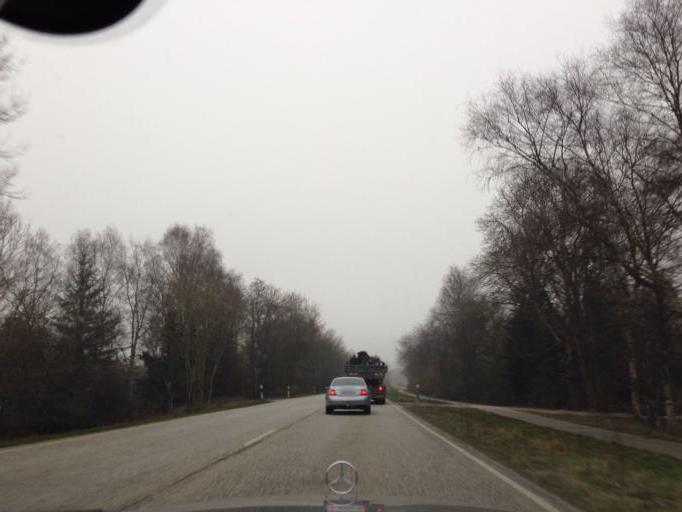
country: DE
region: Schleswig-Holstein
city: Klein Barkau
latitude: 54.2499
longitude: 10.1488
